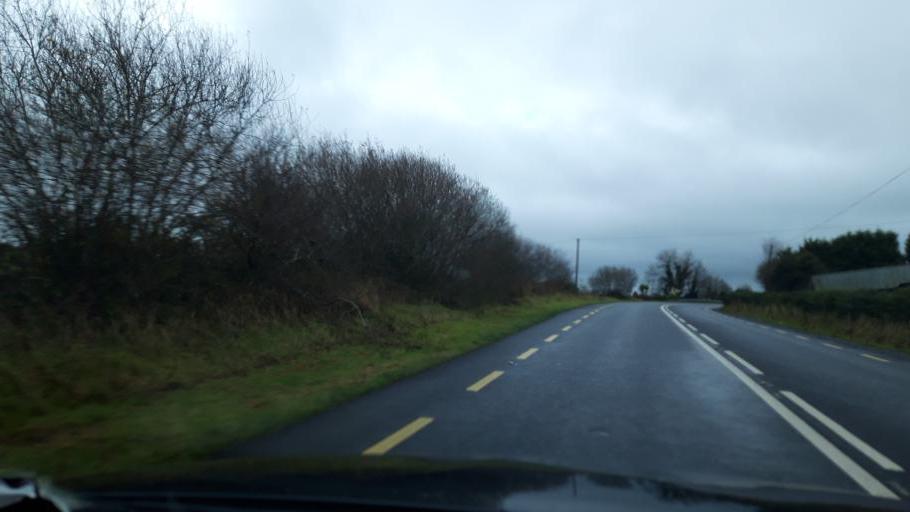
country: IE
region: Ulster
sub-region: County Monaghan
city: Castleblayney
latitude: 54.0870
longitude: -6.6896
